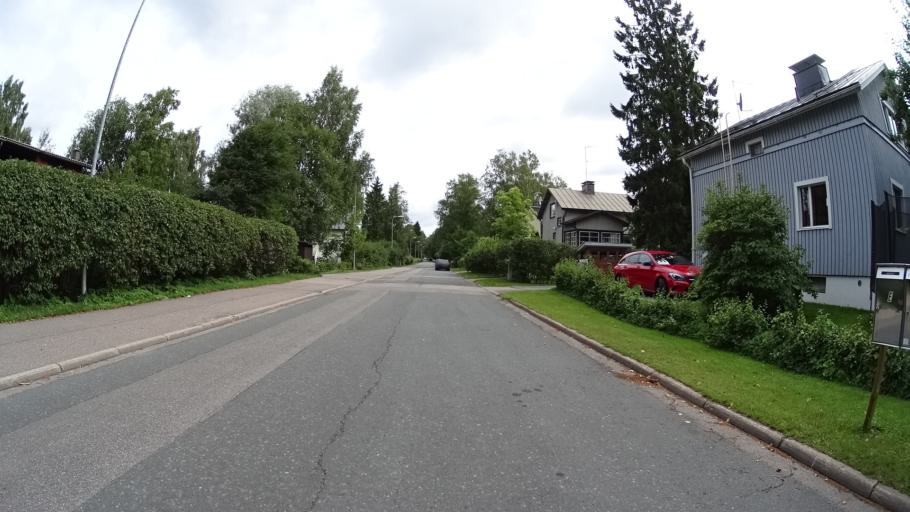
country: FI
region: Uusimaa
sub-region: Helsinki
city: Helsinki
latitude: 60.2534
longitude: 24.9203
